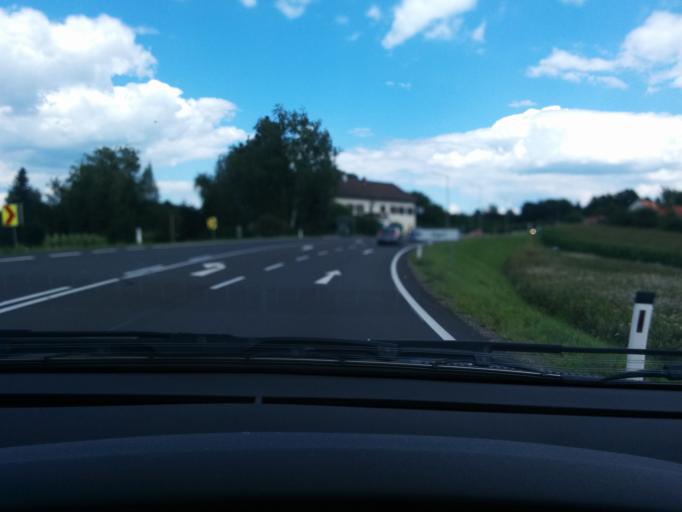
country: AT
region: Styria
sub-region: Politischer Bezirk Weiz
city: Oberrettenbach
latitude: 47.1686
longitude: 15.7782
